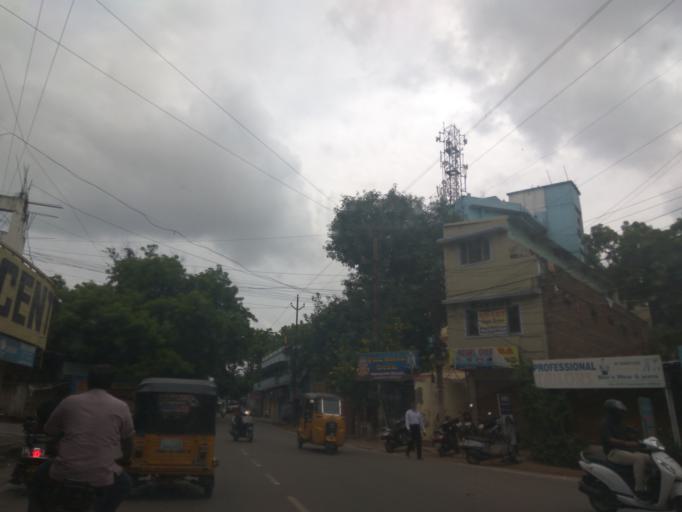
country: IN
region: Telangana
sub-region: Hyderabad
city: Hyderabad
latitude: 17.3958
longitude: 78.4865
